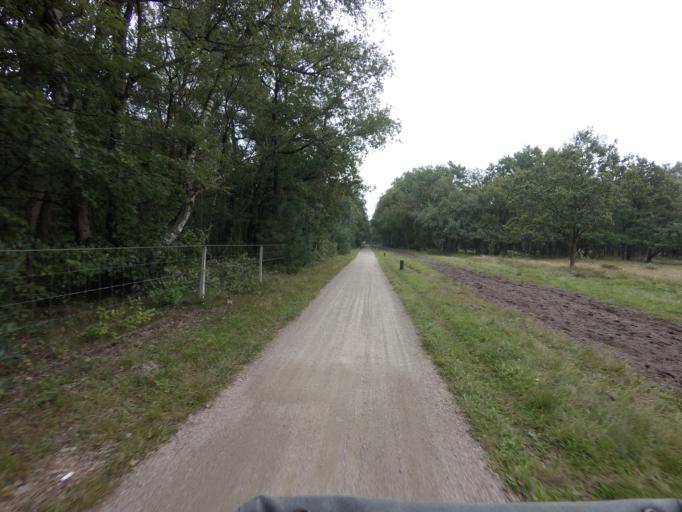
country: NL
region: North Holland
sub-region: Gemeente Wijdemeren
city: Nieuw-Loosdrecht
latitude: 52.1980
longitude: 5.1513
